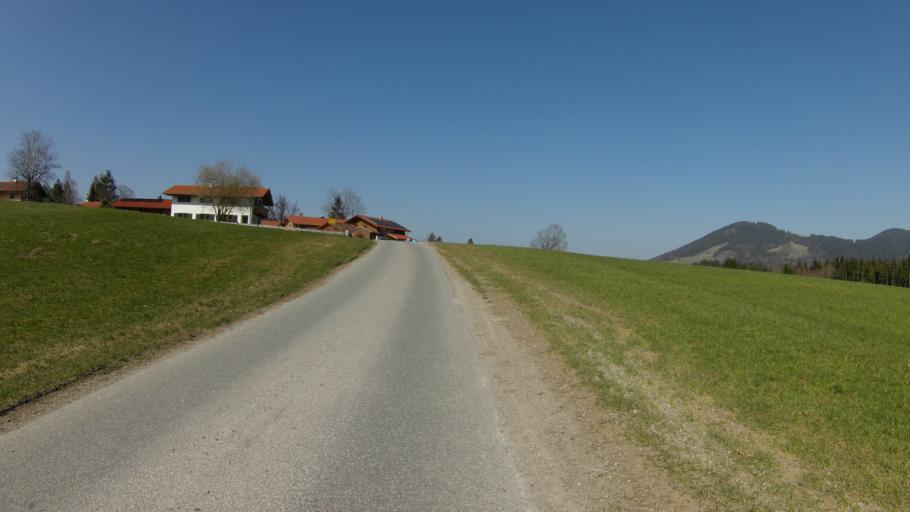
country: DE
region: Bavaria
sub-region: Upper Bavaria
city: Fischbachau
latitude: 47.7238
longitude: 11.9289
